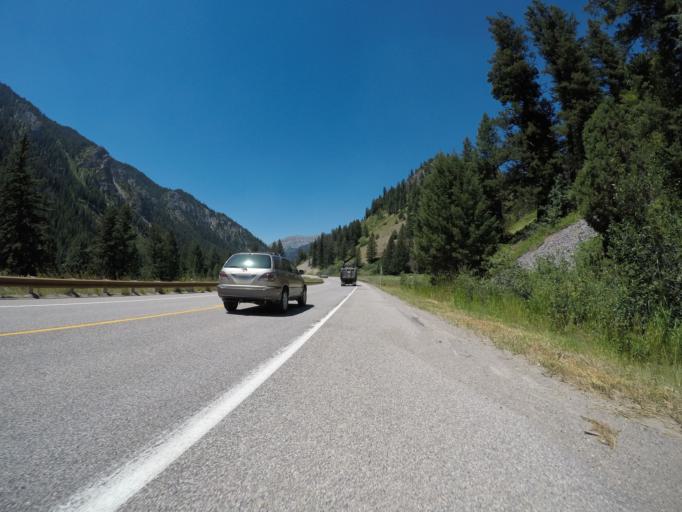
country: US
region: Wyoming
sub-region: Teton County
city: Hoback
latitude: 43.1968
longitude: -110.8820
